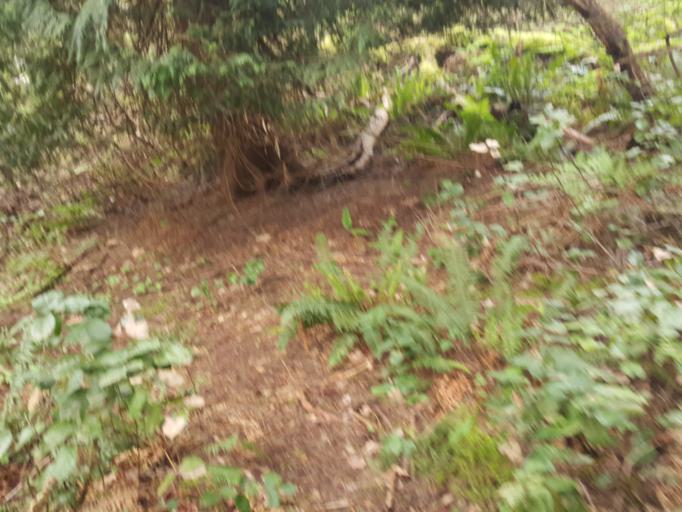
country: US
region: Washington
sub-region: Pierce County
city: University Place
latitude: 47.2057
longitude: -122.5398
